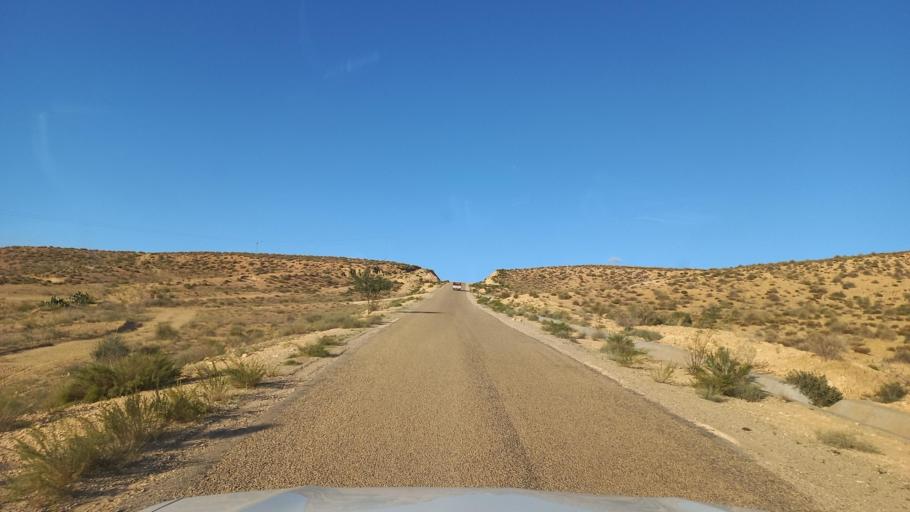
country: TN
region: Al Qasrayn
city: Sbiba
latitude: 35.3473
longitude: 9.1303
